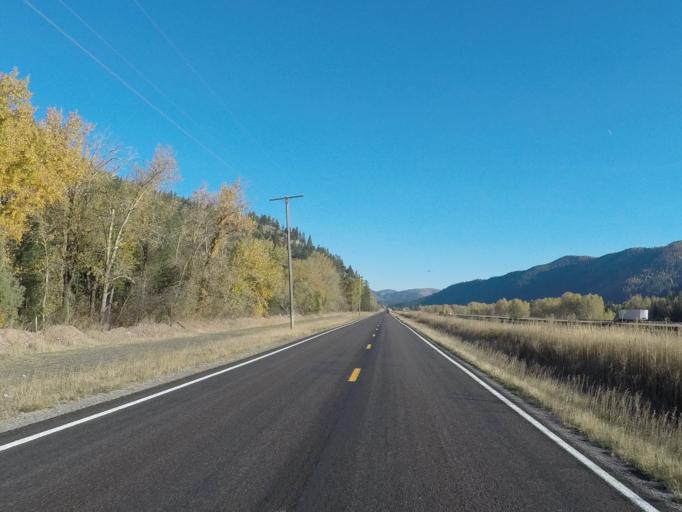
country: US
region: Montana
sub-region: Missoula County
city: Clinton
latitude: 46.8192
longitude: -113.7987
